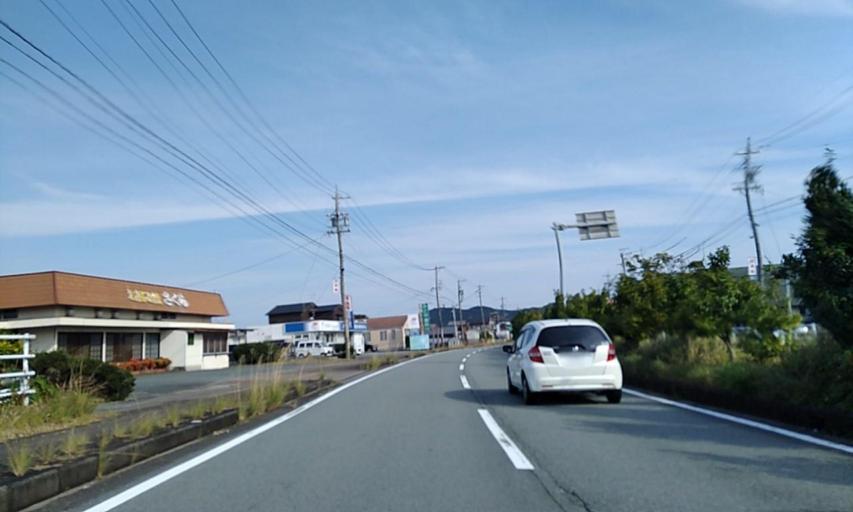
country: JP
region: Mie
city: Ise
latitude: 34.5056
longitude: 136.7584
